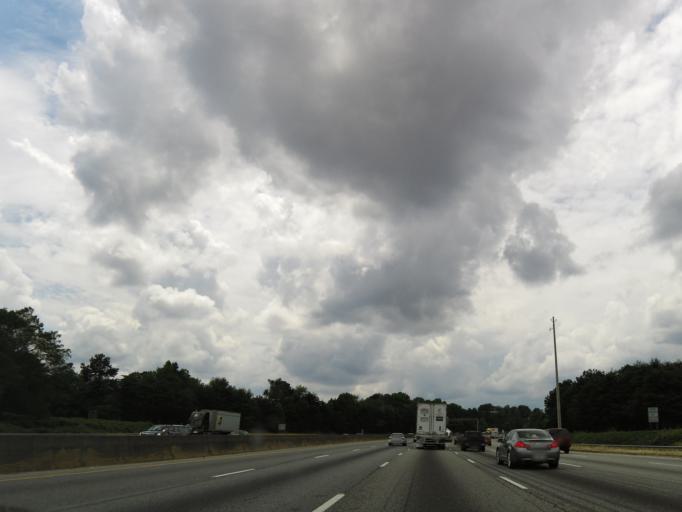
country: US
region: Georgia
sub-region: Fulton County
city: College Park
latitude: 33.6168
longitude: -84.4396
